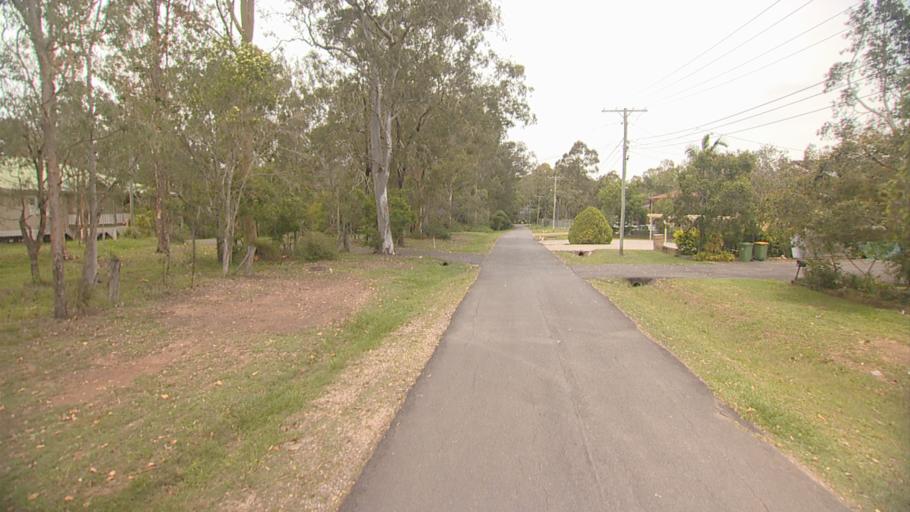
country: AU
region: Queensland
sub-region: Logan
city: Slacks Creek
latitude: -27.6494
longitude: 153.1525
